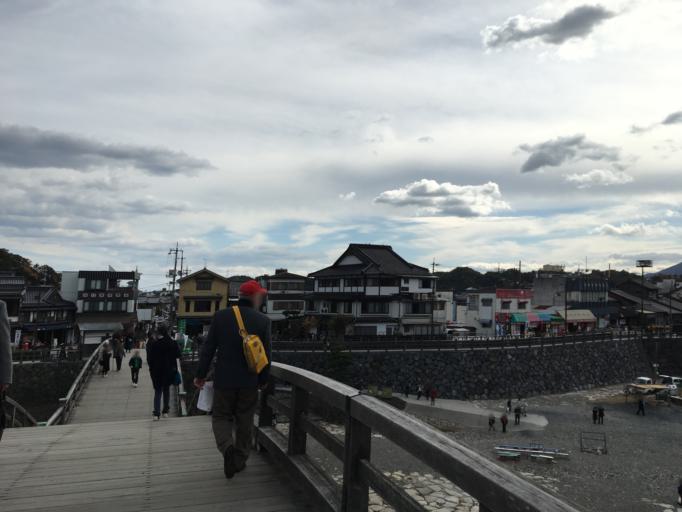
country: JP
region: Yamaguchi
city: Iwakuni
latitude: 34.1675
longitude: 132.1786
